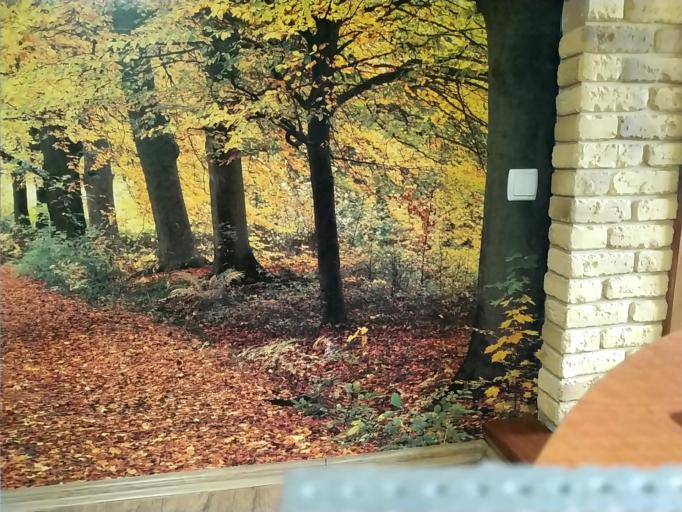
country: RU
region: Tverskaya
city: Kalashnikovo
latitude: 57.2742
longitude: 35.2451
